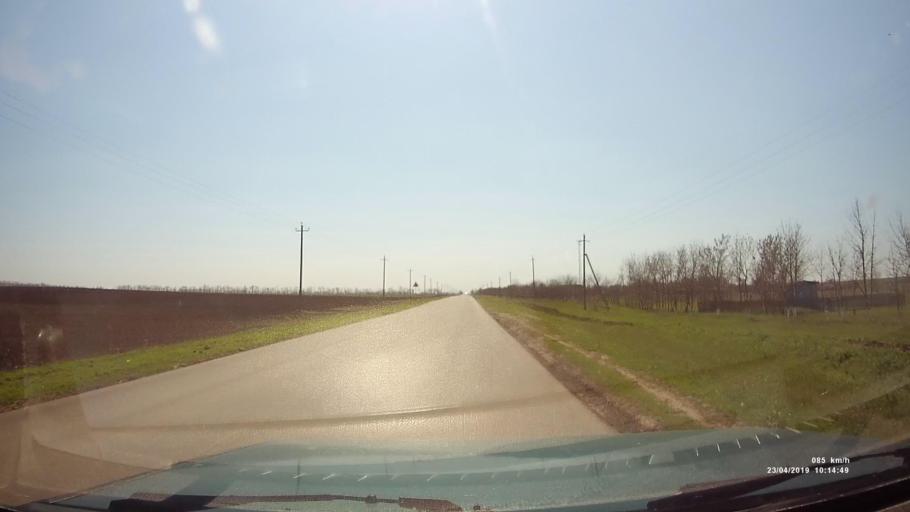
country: RU
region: Rostov
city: Sovetskoye
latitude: 46.6735
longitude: 42.3746
